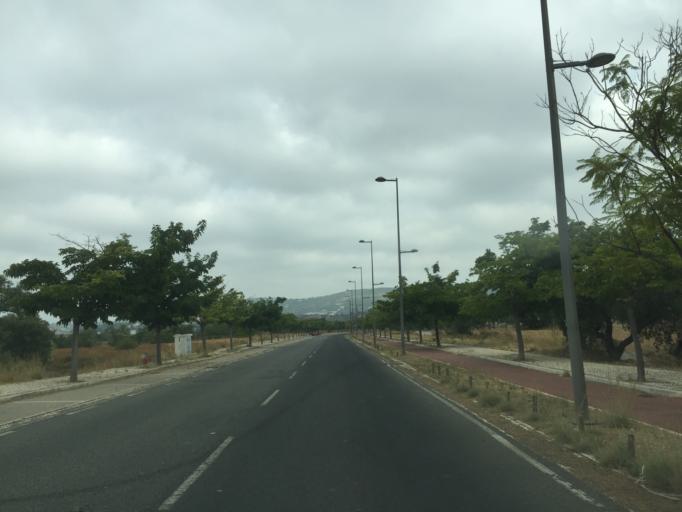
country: PT
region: Faro
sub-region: Faro
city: Santa Barbara de Nexe
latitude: 37.0800
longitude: -7.9768
